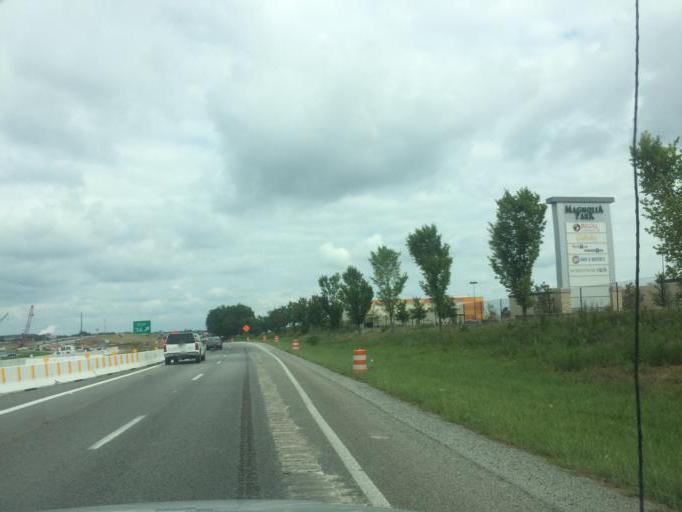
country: US
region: South Carolina
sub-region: Greenville County
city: Mauldin
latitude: 34.8354
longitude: -82.3060
